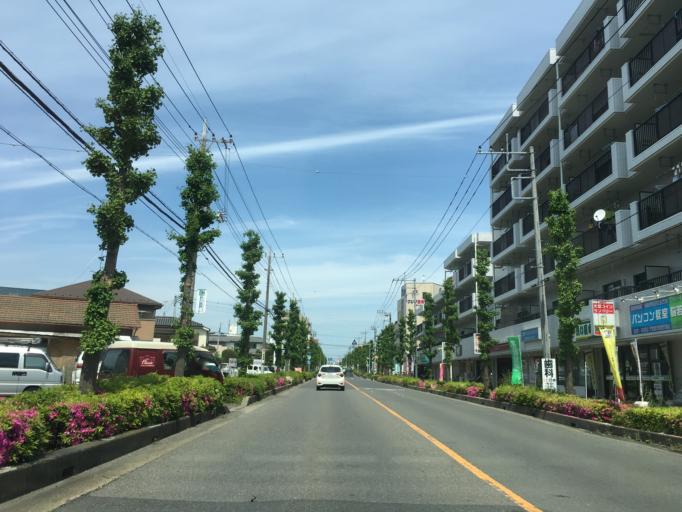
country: JP
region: Saitama
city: Ageoshimo
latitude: 35.9744
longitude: 139.5827
